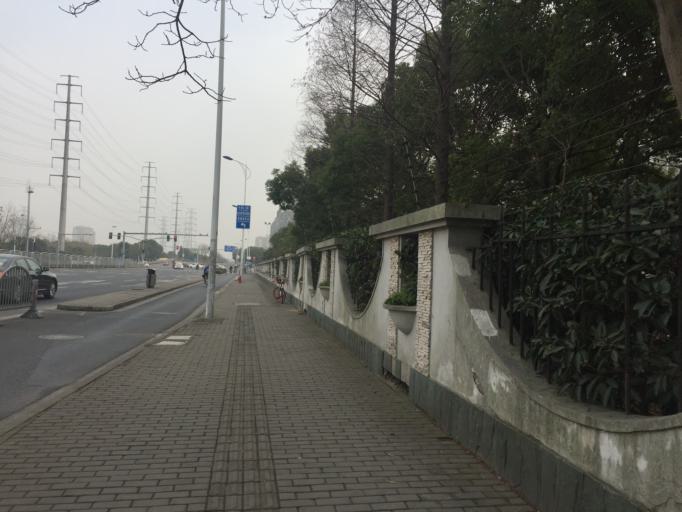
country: CN
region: Shanghai Shi
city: Huamu
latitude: 31.1895
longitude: 121.5341
